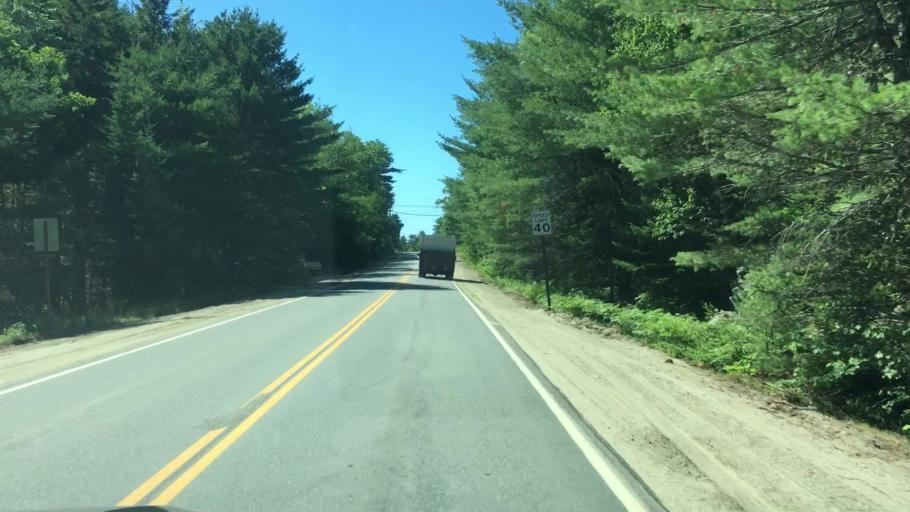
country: US
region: Maine
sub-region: Hancock County
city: Sedgwick
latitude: 44.3724
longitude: -68.5674
